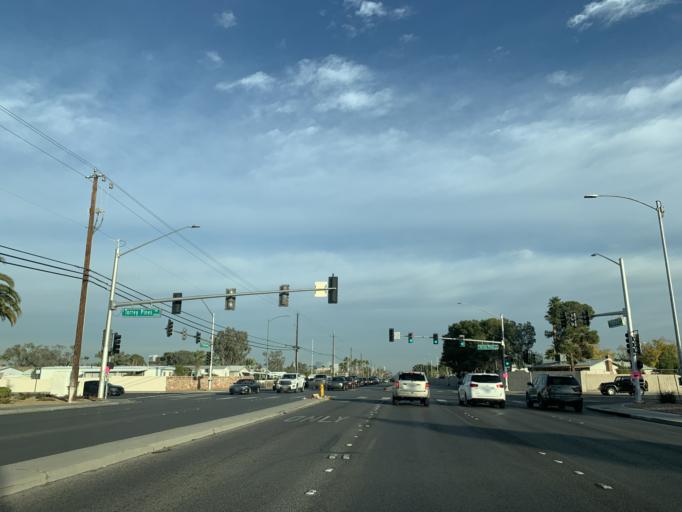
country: US
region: Nevada
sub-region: Clark County
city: Spring Valley
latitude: 36.0998
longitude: -115.2346
